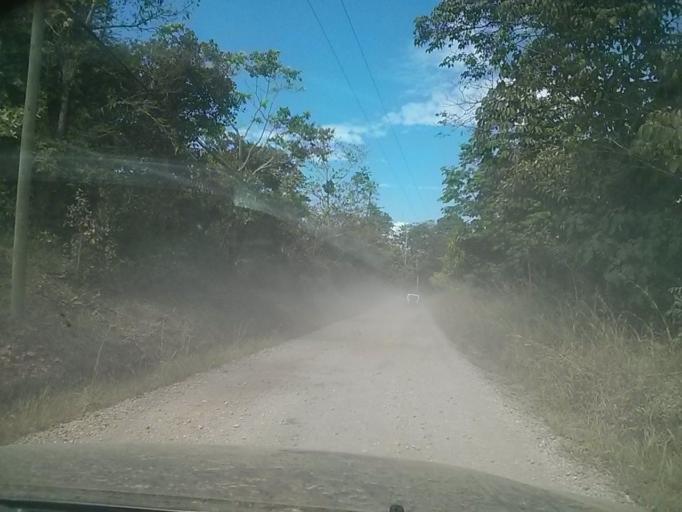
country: CR
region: Puntarenas
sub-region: Canton de Golfito
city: Golfito
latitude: 8.4522
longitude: -83.0568
